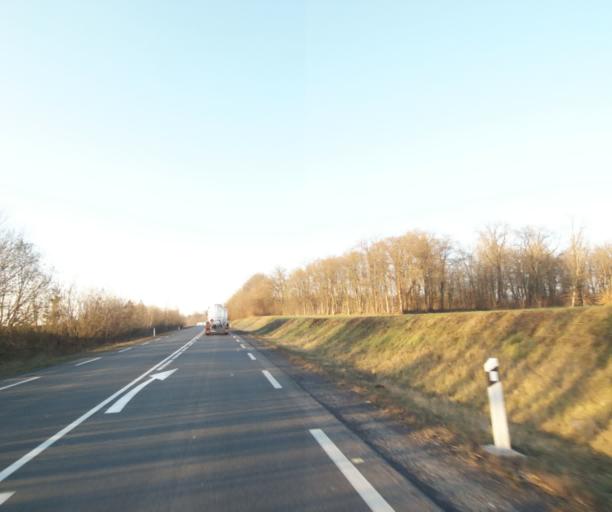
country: FR
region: Champagne-Ardenne
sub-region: Departement de la Haute-Marne
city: Bienville
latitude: 48.5496
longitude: 5.0650
